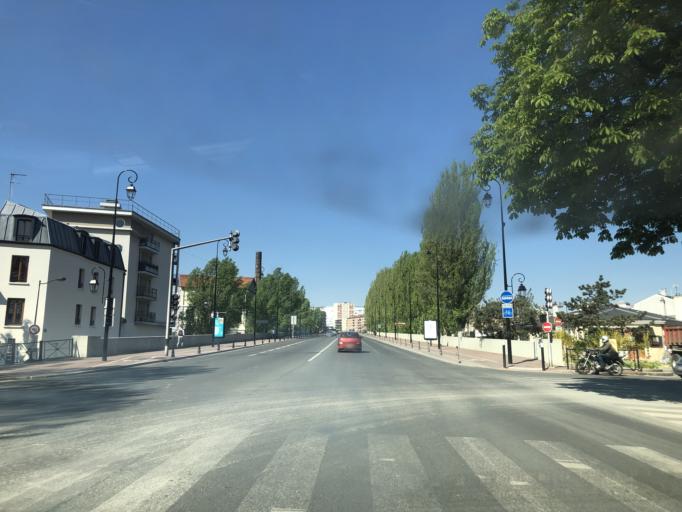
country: FR
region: Ile-de-France
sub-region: Departement du Val-de-Marne
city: Joinville-le-Pont
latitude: 48.8202
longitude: 2.4737
